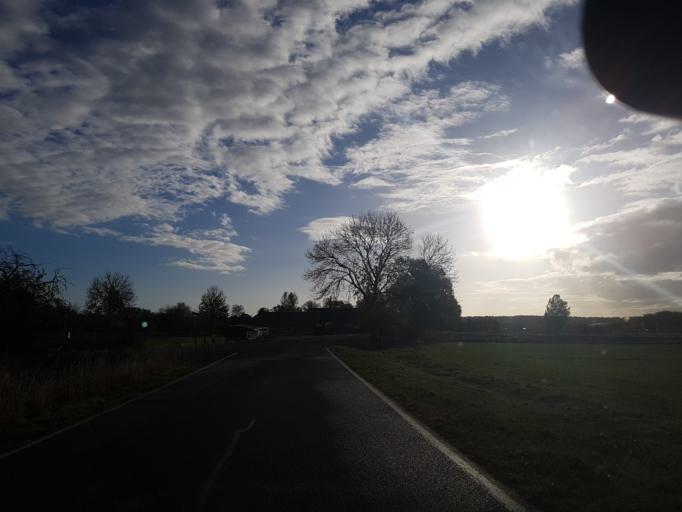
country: DE
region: Brandenburg
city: Nauen
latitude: 52.6862
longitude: 12.9287
